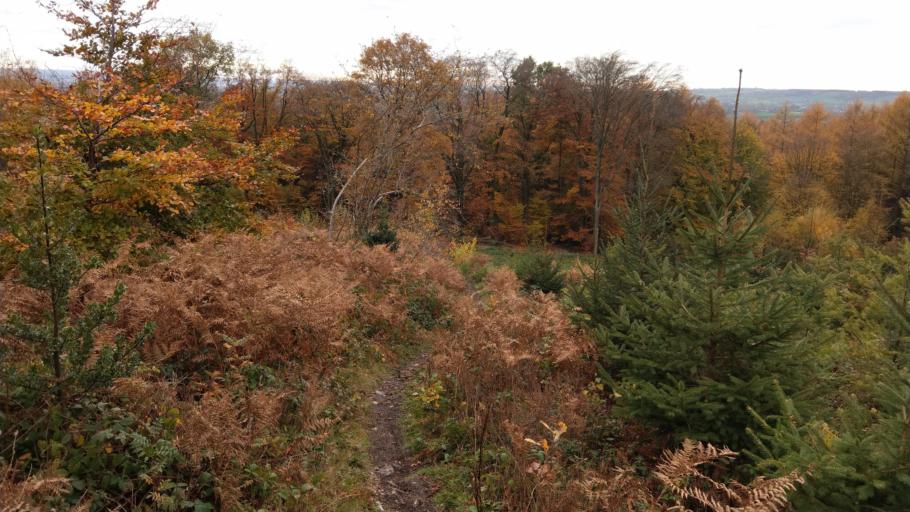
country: BE
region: Wallonia
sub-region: Province de Liege
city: La Calamine
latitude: 50.7393
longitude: 6.0137
